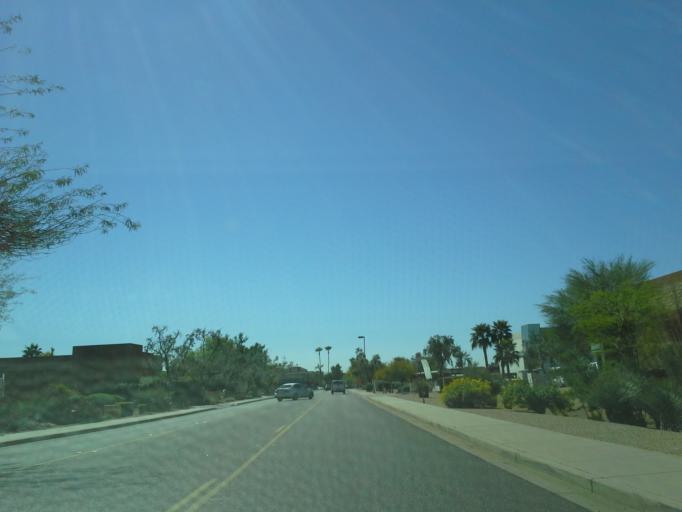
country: US
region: Arizona
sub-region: Maricopa County
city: Paradise Valley
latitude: 33.6210
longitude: -111.9012
